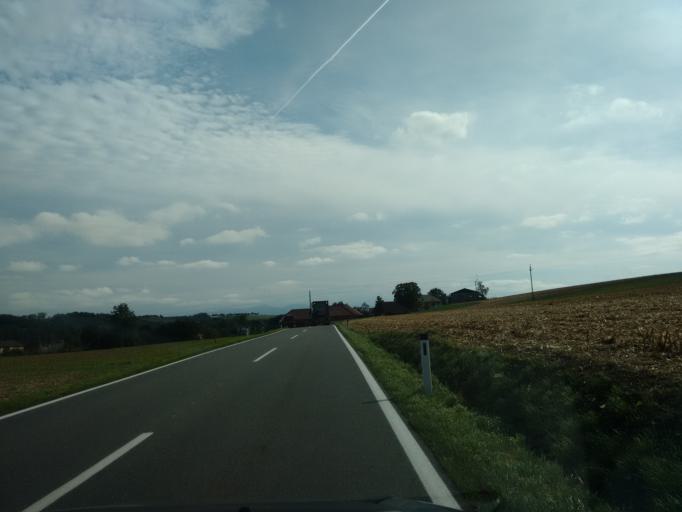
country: AT
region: Upper Austria
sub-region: Politischer Bezirk Steyr-Land
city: Bad Hall
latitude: 48.0937
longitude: 14.1912
